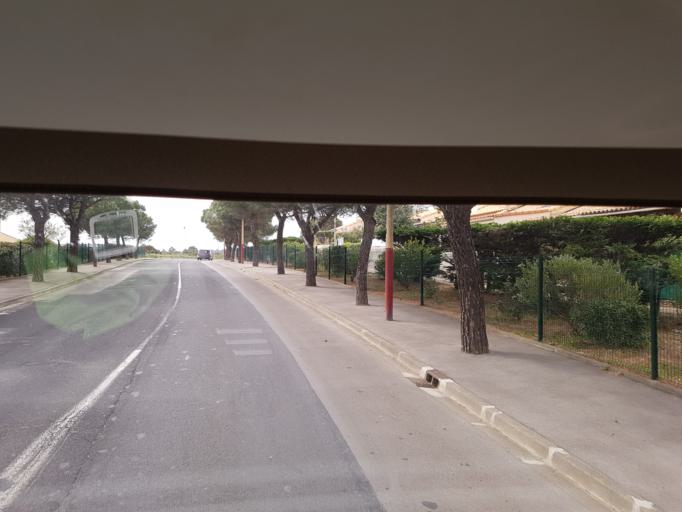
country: FR
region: Languedoc-Roussillon
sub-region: Departement de l'Aude
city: Fleury
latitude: 43.1817
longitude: 3.1842
